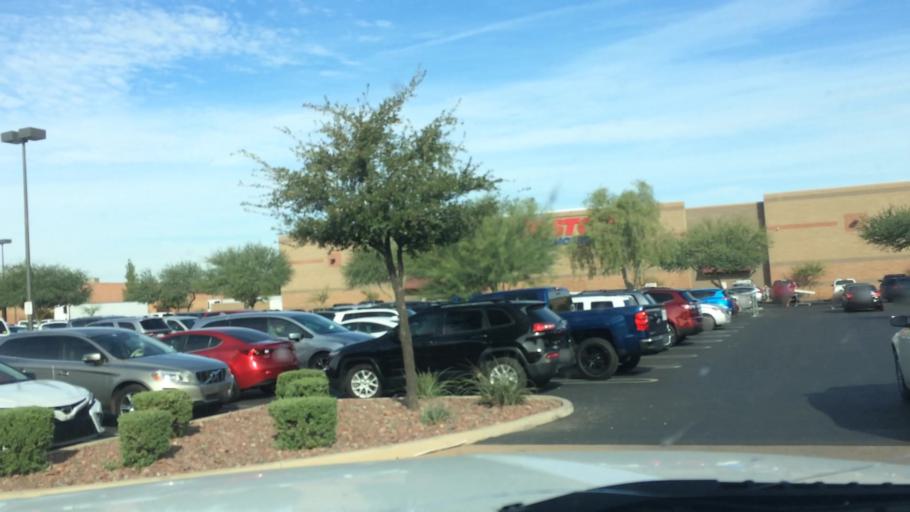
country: US
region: Arizona
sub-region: Maricopa County
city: Tolleson
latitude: 33.4665
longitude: -112.2749
